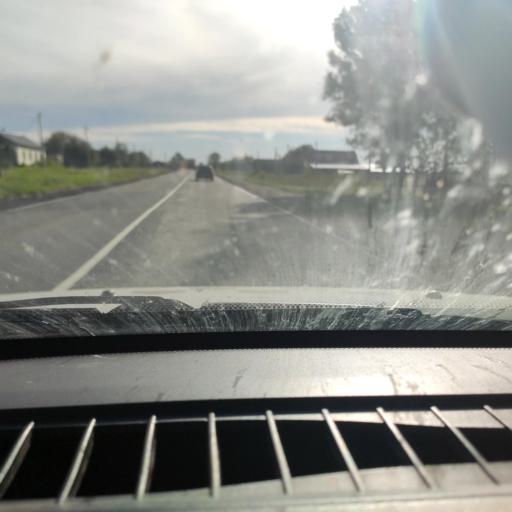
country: RU
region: Kirov
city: Vakhrushi
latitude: 58.6734
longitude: 49.9488
